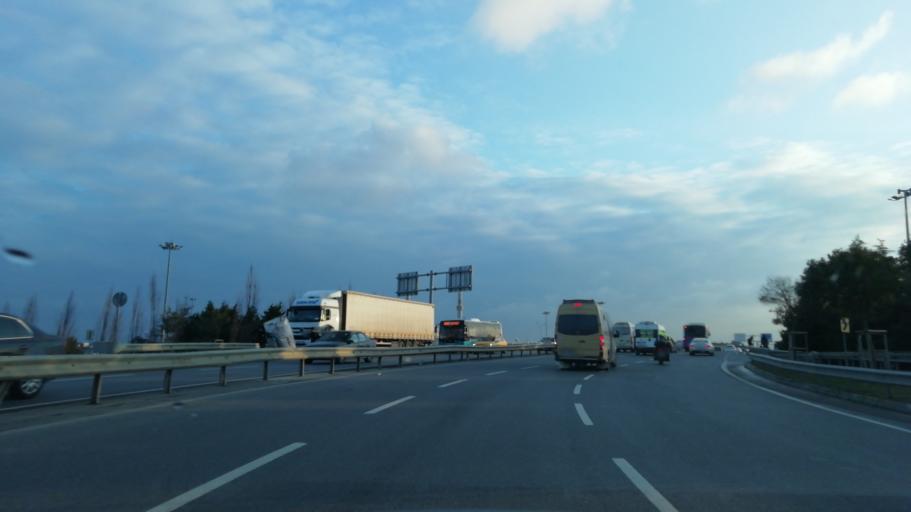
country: TR
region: Istanbul
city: Yakuplu
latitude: 40.9869
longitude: 28.7227
